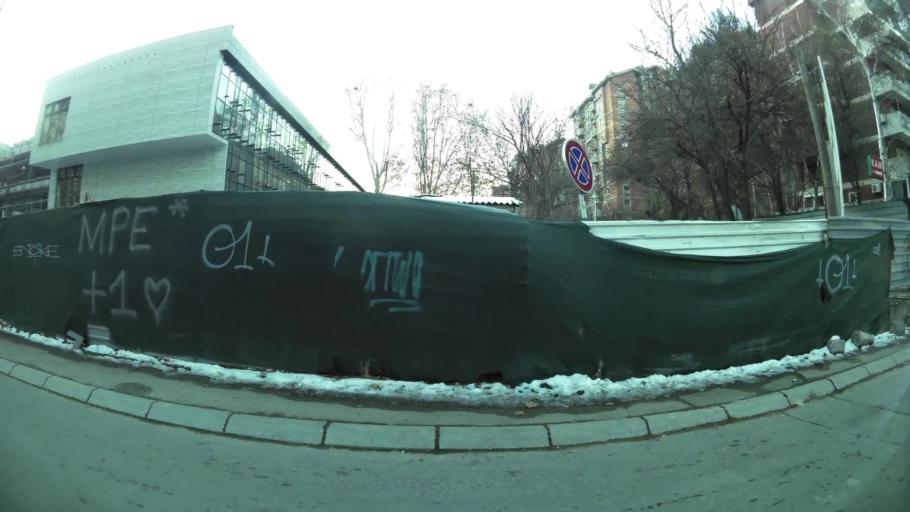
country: MK
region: Karpos
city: Skopje
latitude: 41.9930
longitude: 21.4150
